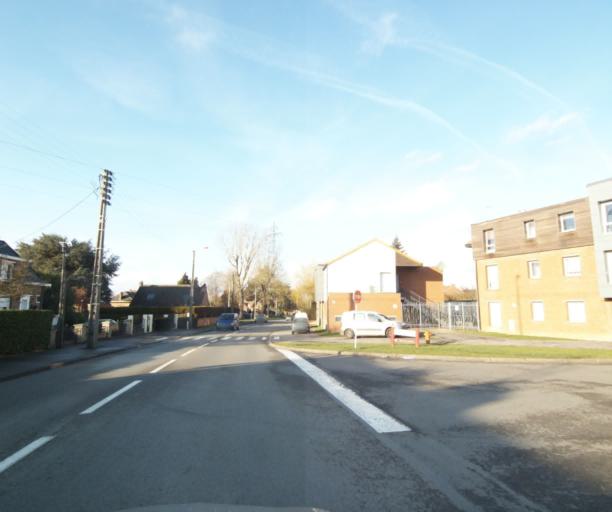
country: FR
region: Nord-Pas-de-Calais
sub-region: Departement du Nord
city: Marly
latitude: 50.3389
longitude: 3.5516
